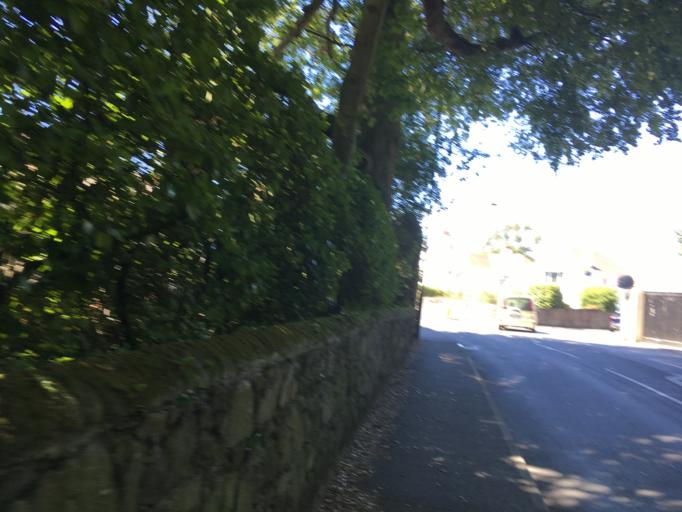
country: GG
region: St Peter Port
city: Saint Peter Port
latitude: 49.4584
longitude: -2.5530
